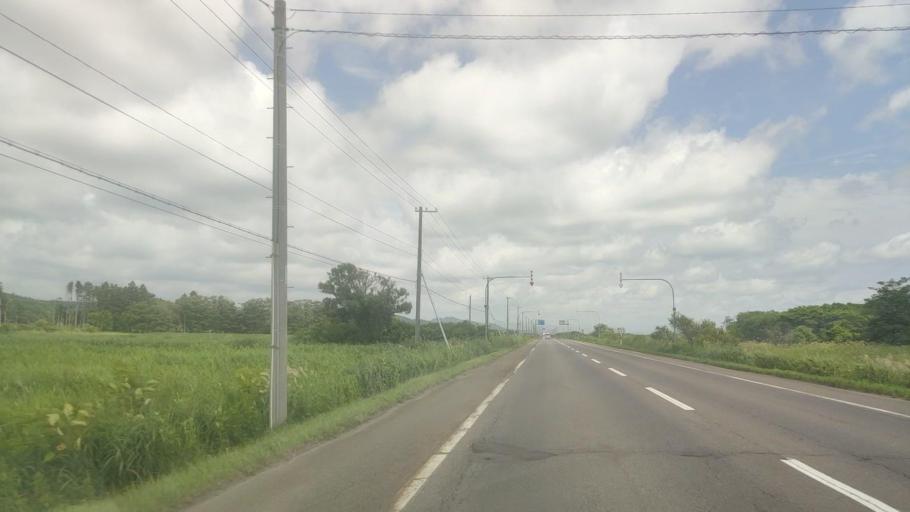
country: JP
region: Hokkaido
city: Niseko Town
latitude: 42.3898
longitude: 140.2978
